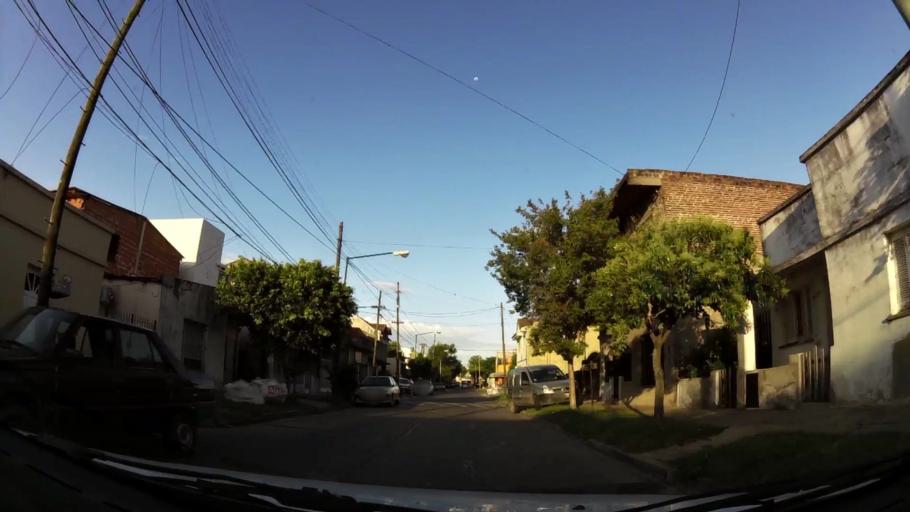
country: AR
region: Buenos Aires
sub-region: Partido de San Isidro
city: San Isidro
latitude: -34.4674
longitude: -58.5458
